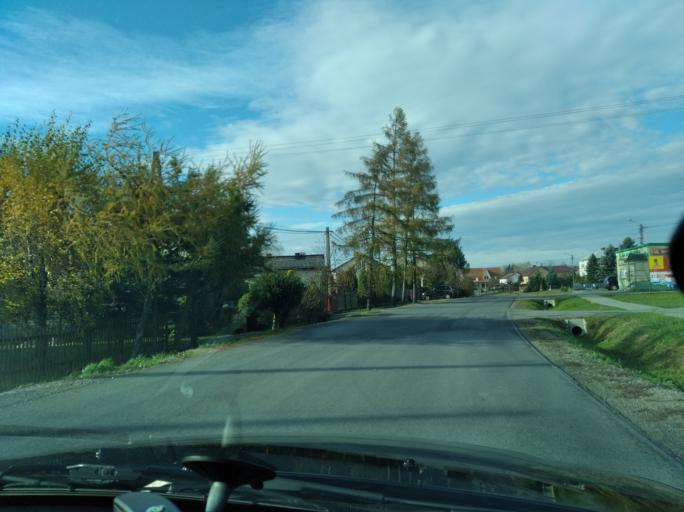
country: PL
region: Subcarpathian Voivodeship
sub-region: Powiat ropczycko-sedziszowski
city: Sedziszow Malopolski
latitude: 50.0781
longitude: 21.7409
